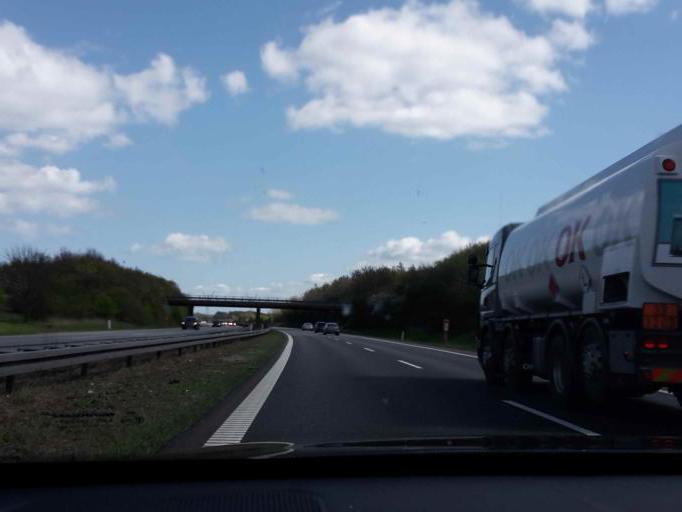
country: DK
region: South Denmark
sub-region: Fredericia Kommune
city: Taulov
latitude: 55.5385
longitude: 9.6353
